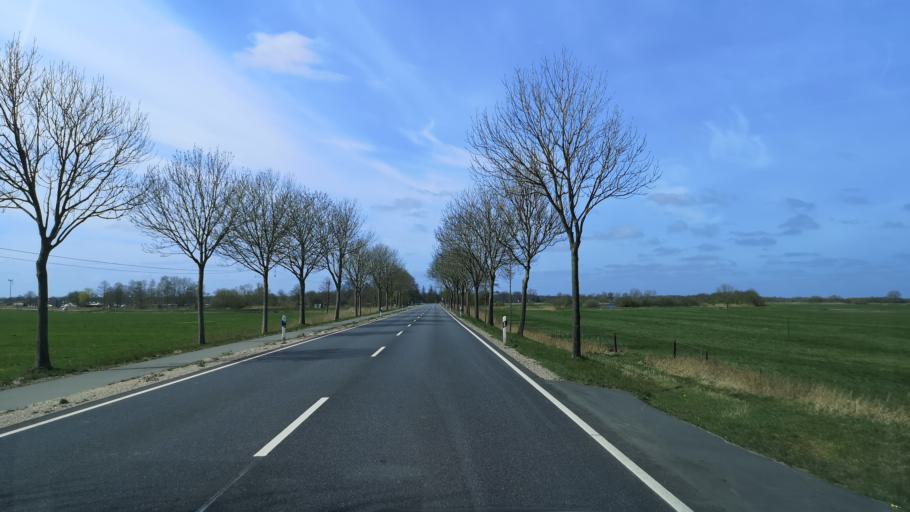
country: DE
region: Schleswig-Holstein
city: Prinzenmoor
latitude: 54.2229
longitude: 9.4480
